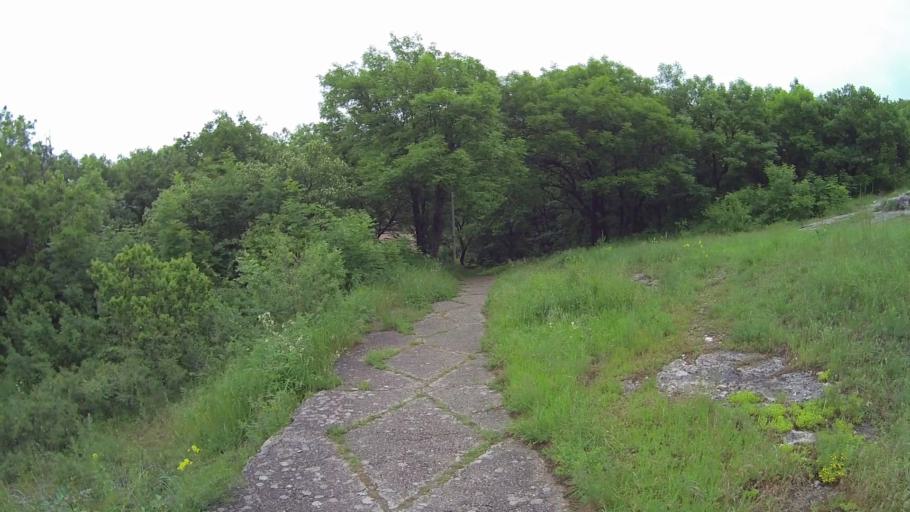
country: RU
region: Stavropol'skiy
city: Goryachevodskiy
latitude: 44.0399
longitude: 43.0838
